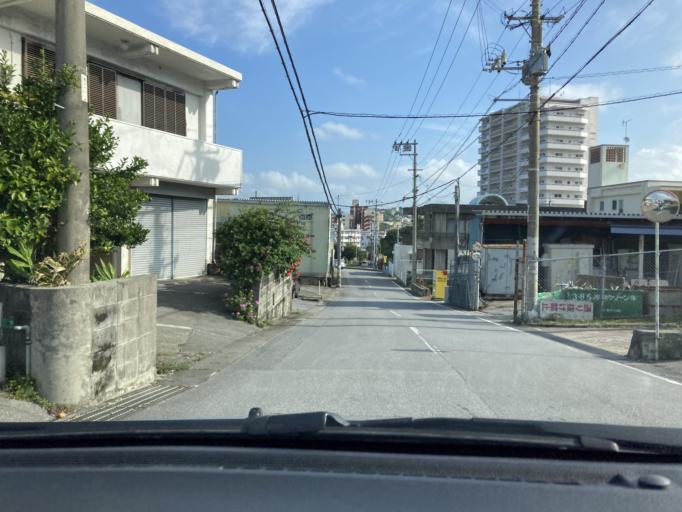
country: JP
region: Okinawa
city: Ginowan
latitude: 26.2346
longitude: 127.7450
